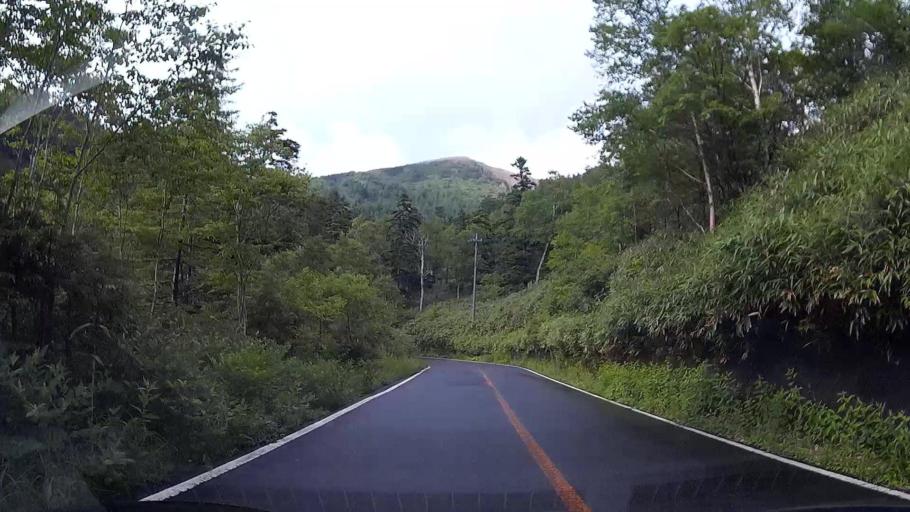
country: JP
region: Nagano
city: Nakano
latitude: 36.6371
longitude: 138.5223
